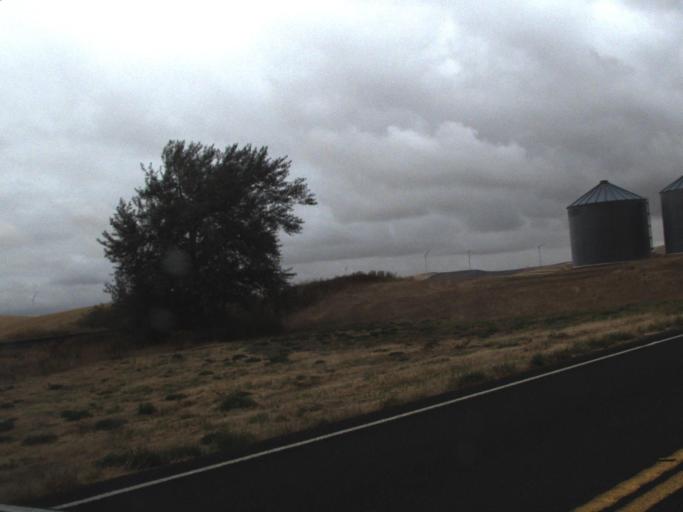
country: US
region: Washington
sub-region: Whitman County
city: Colfax
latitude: 47.1636
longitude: -117.2791
